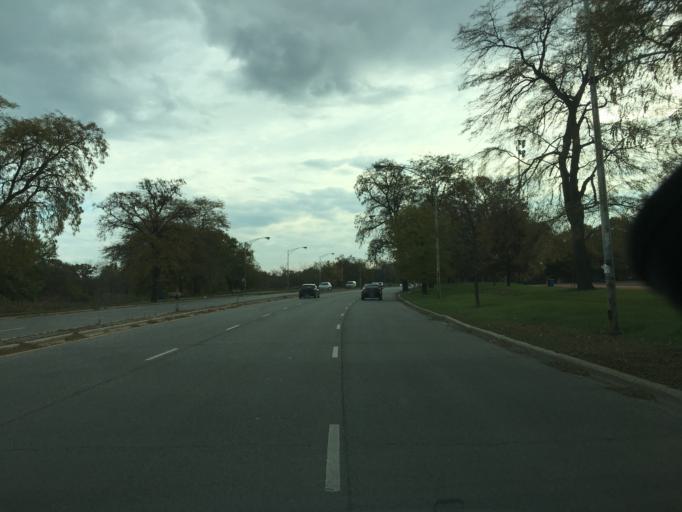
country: US
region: Illinois
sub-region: Cook County
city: Chicago
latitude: 41.7854
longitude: -87.5849
